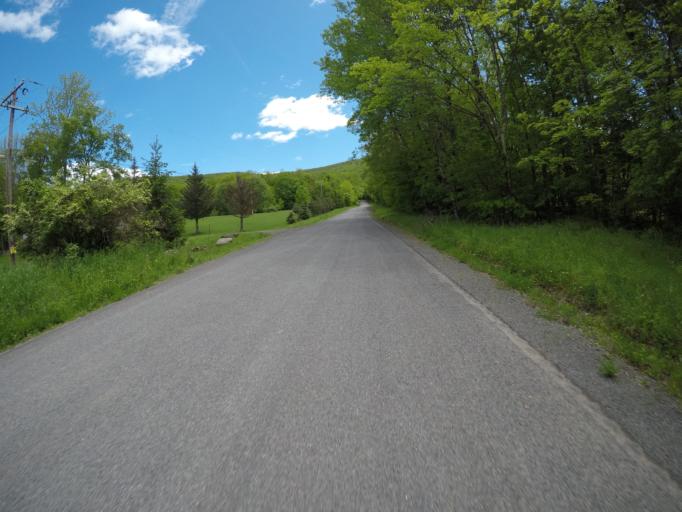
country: US
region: New York
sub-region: Delaware County
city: Stamford
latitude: 42.2792
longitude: -74.5065
